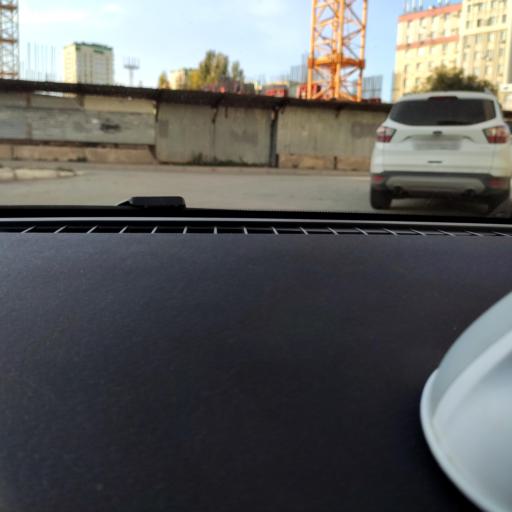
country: RU
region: Samara
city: Samara
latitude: 53.2119
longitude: 50.2167
